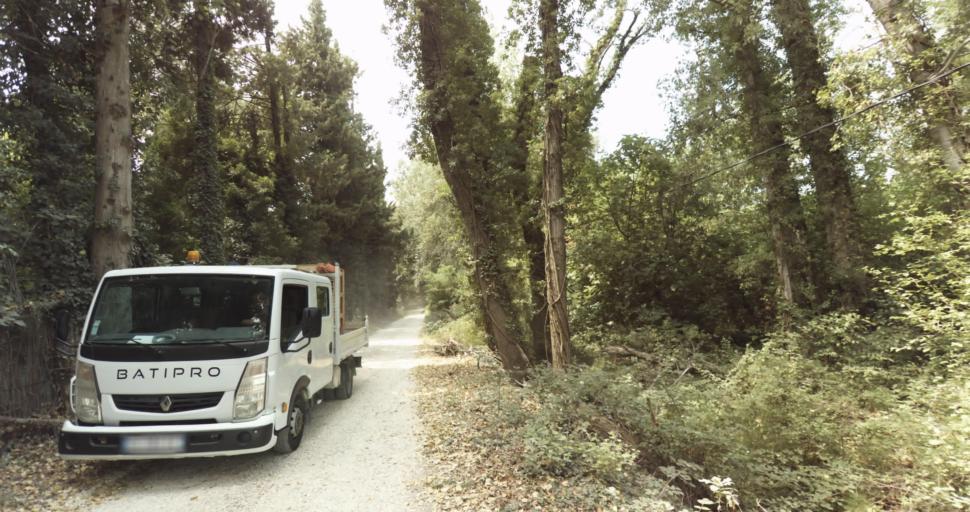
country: FR
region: Provence-Alpes-Cote d'Azur
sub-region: Departement du Vaucluse
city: Loriol-du-Comtat
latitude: 44.0586
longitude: 4.9869
